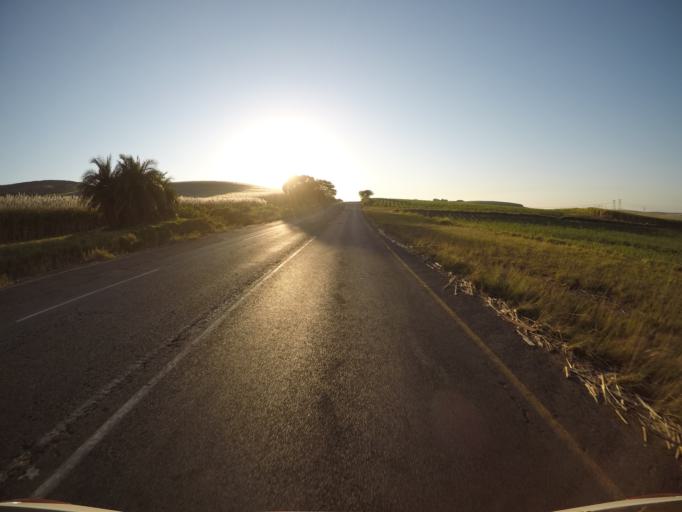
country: ZA
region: KwaZulu-Natal
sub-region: uThungulu District Municipality
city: Eshowe
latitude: -28.9501
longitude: 31.6727
